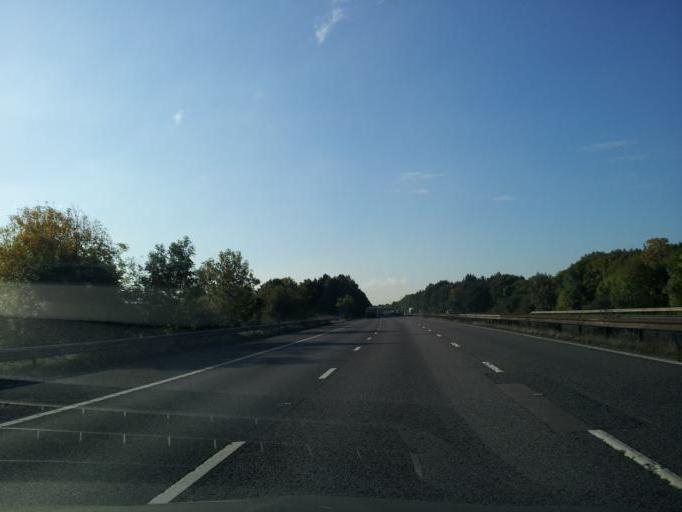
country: GB
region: England
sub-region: Leicestershire
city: Broughton Astley
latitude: 52.5005
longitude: -1.1893
